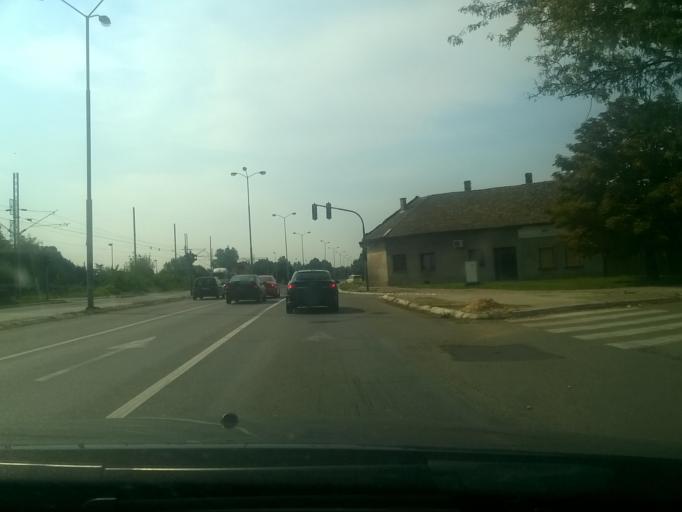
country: RS
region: Autonomna Pokrajina Vojvodina
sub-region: Juznobanatski Okrug
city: Pancevo
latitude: 44.8621
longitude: 20.6574
